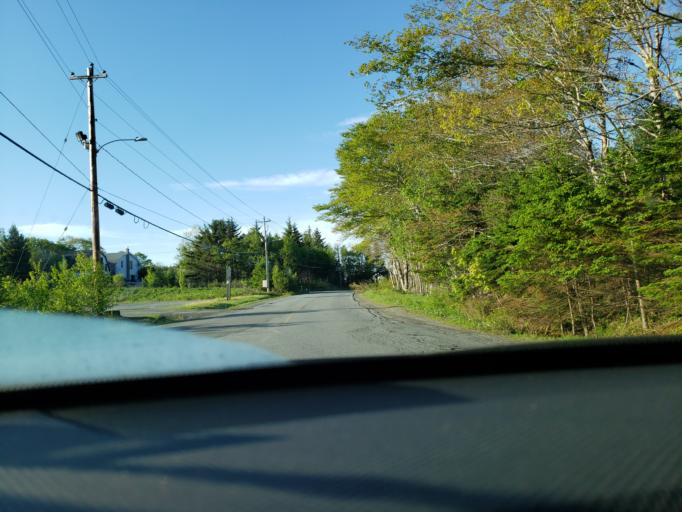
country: CA
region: Nova Scotia
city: Cole Harbour
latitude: 44.7409
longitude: -63.3811
